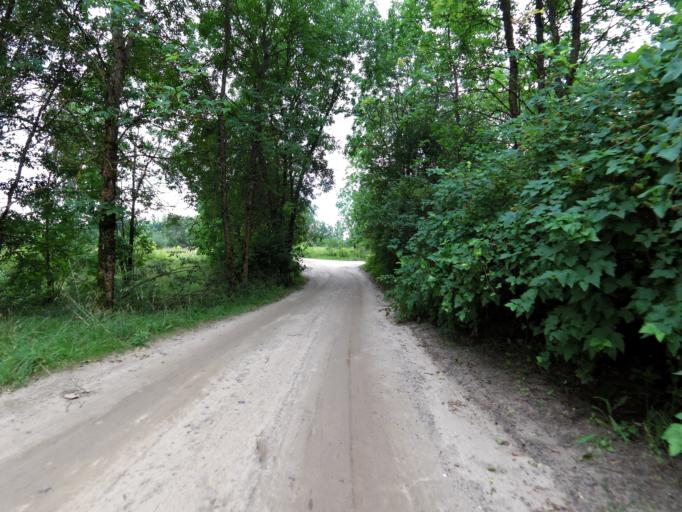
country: LT
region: Vilnius County
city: Naujamiestis
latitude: 54.6578
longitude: 25.2878
